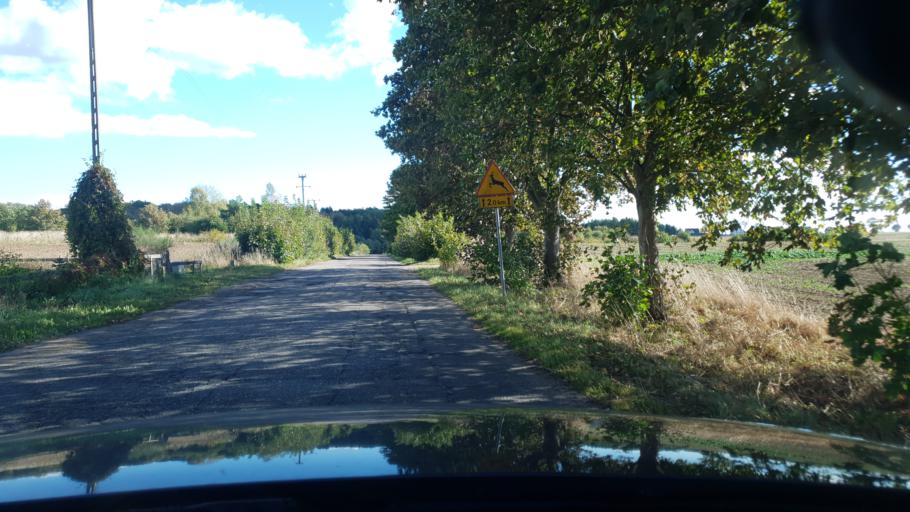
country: PL
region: Pomeranian Voivodeship
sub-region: Powiat pucki
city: Zelistrzewo
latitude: 54.6905
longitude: 18.4190
